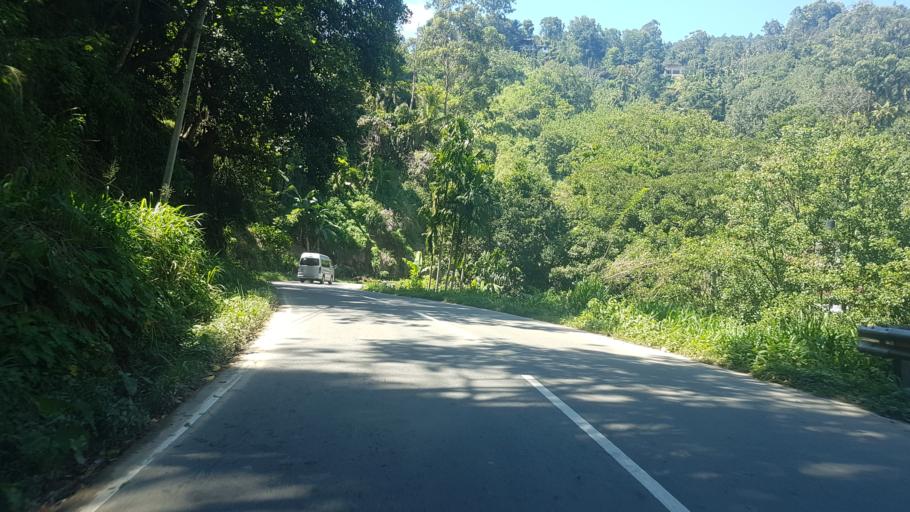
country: LK
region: Uva
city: Badulla
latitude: 6.8674
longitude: 81.0477
